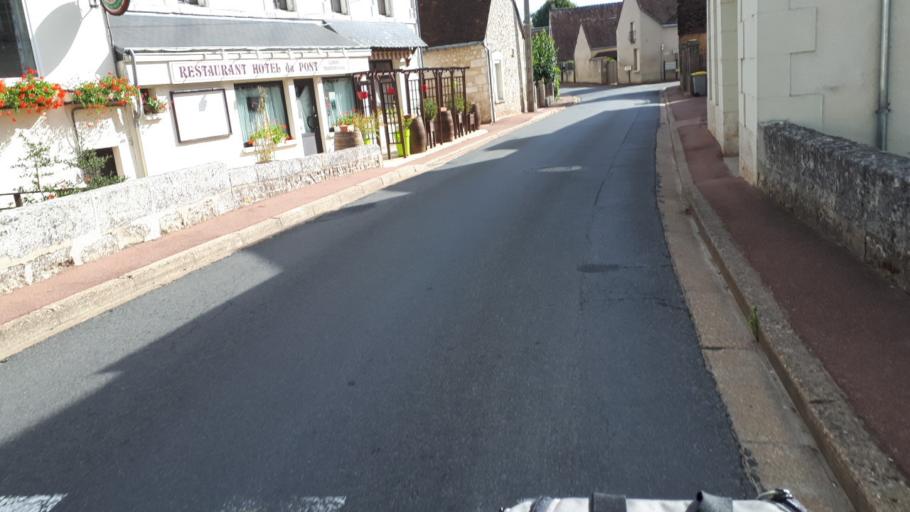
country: FR
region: Centre
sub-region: Departement du Loir-et-Cher
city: Villiers-sur-Loir
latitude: 47.7873
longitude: 0.9636
